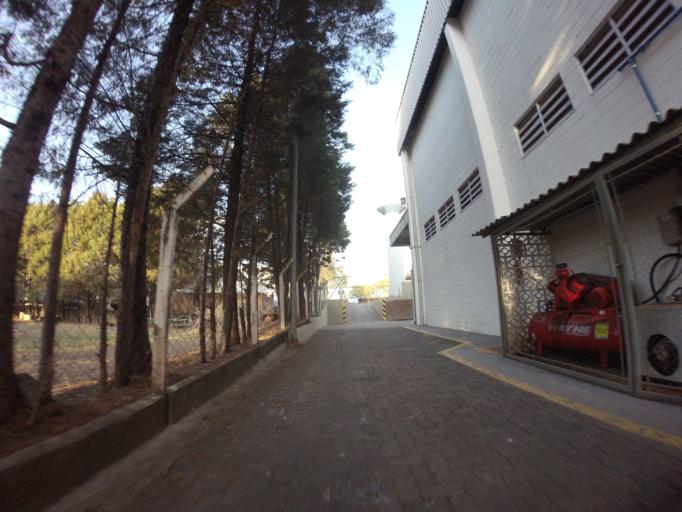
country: BR
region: Sao Paulo
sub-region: Piracicaba
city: Piracicaba
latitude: -22.7333
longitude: -47.5956
